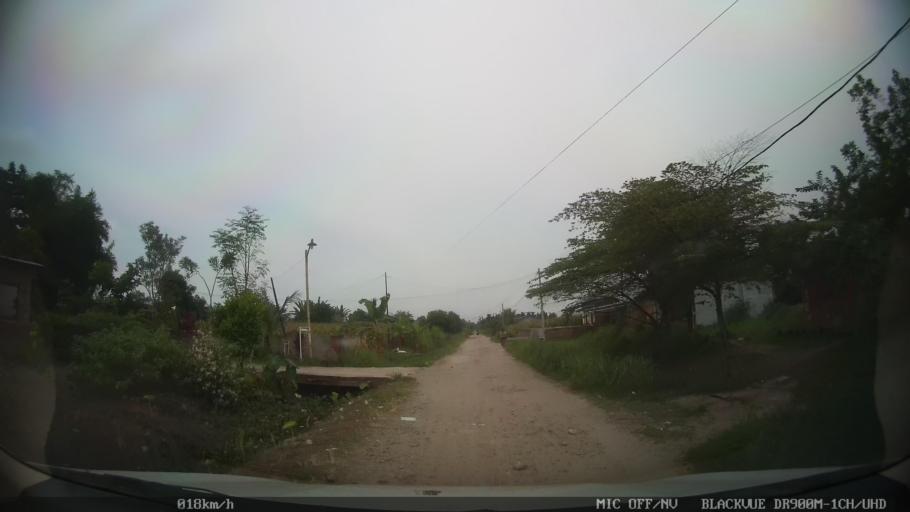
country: ID
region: North Sumatra
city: Medan
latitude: 3.5735
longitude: 98.7353
